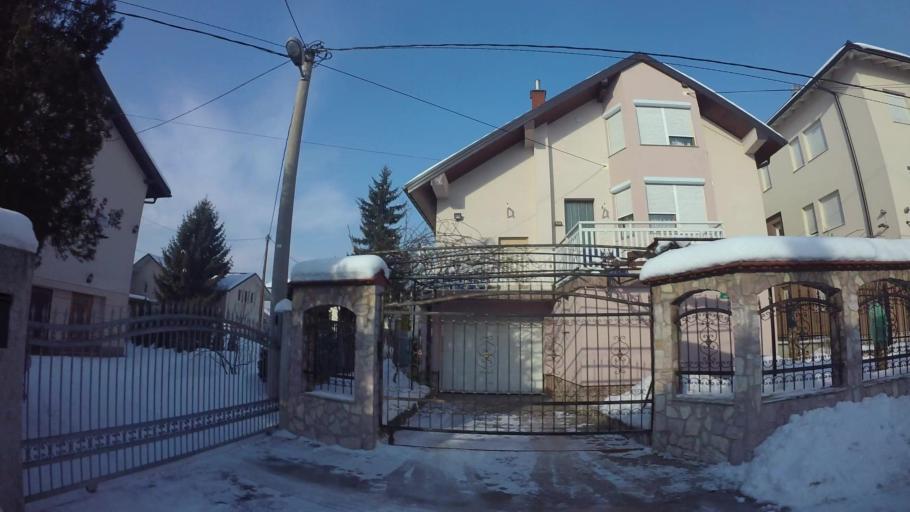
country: BA
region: Federation of Bosnia and Herzegovina
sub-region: Kanton Sarajevo
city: Sarajevo
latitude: 43.8369
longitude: 18.3391
